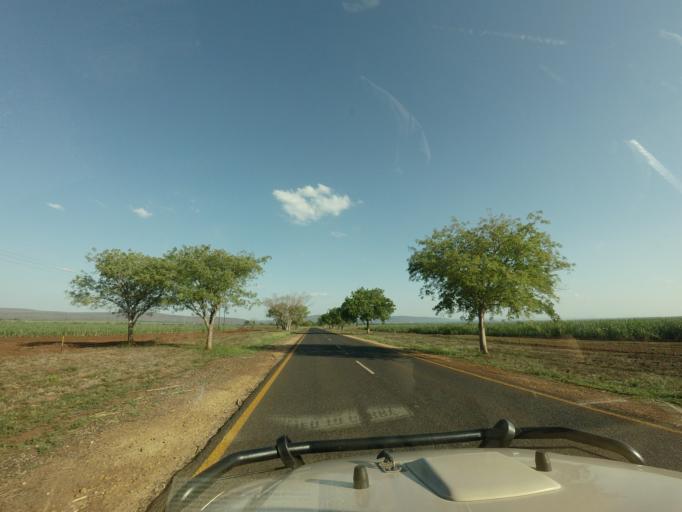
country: ZA
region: Mpumalanga
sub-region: Ehlanzeni District
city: Komatipoort
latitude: -25.4038
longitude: 31.9254
